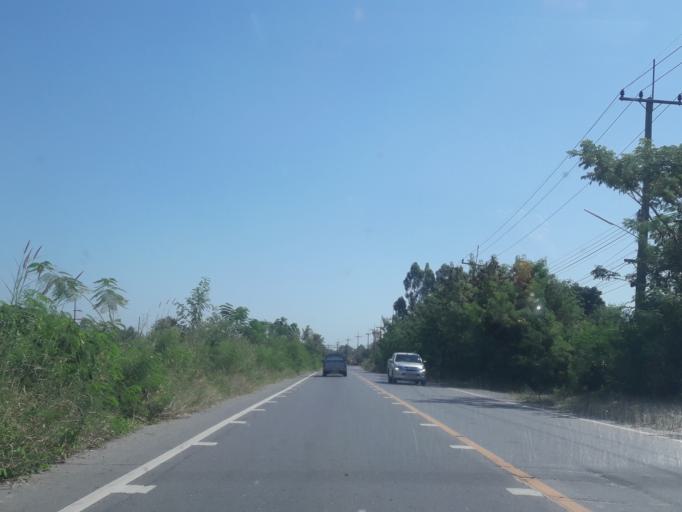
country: TH
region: Sara Buri
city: Nong Khae
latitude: 14.3164
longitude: 100.8605
